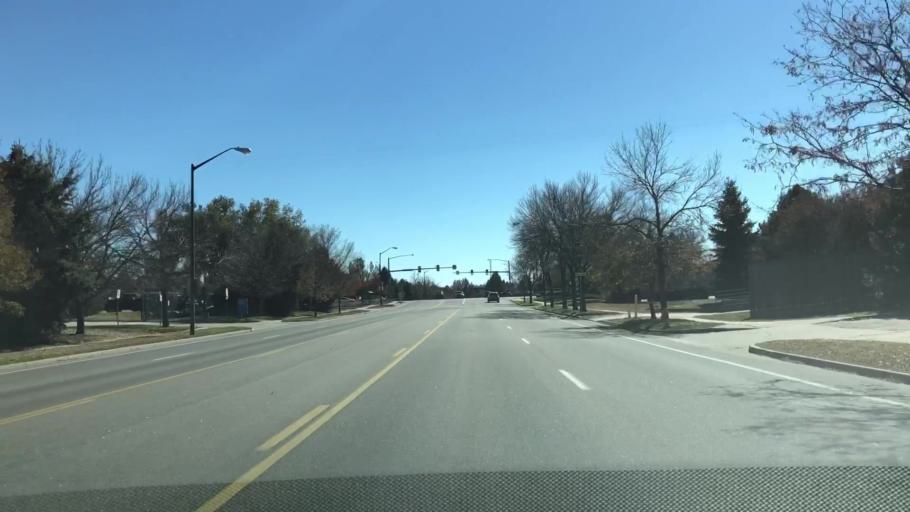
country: US
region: Colorado
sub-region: Larimer County
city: Fort Collins
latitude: 40.5306
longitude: -105.0742
